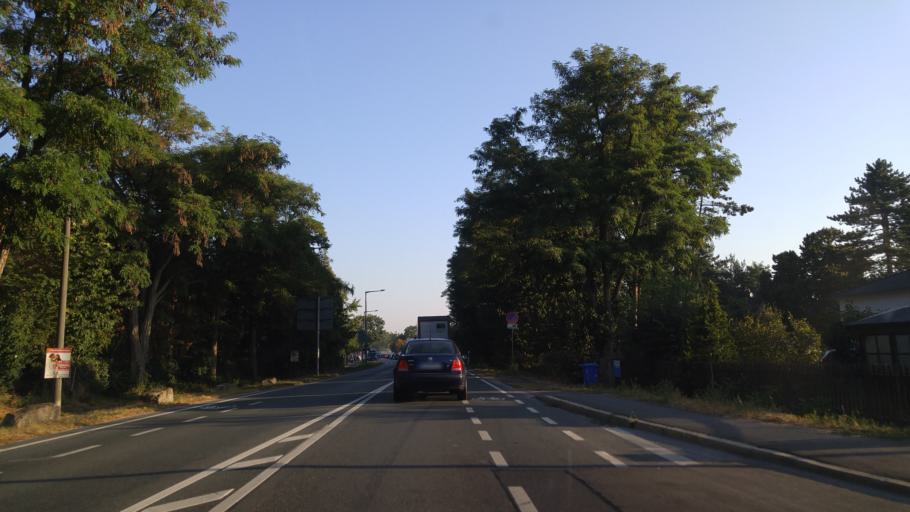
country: DE
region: Bavaria
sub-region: Regierungsbezirk Mittelfranken
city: Furth
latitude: 49.5138
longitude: 10.9751
